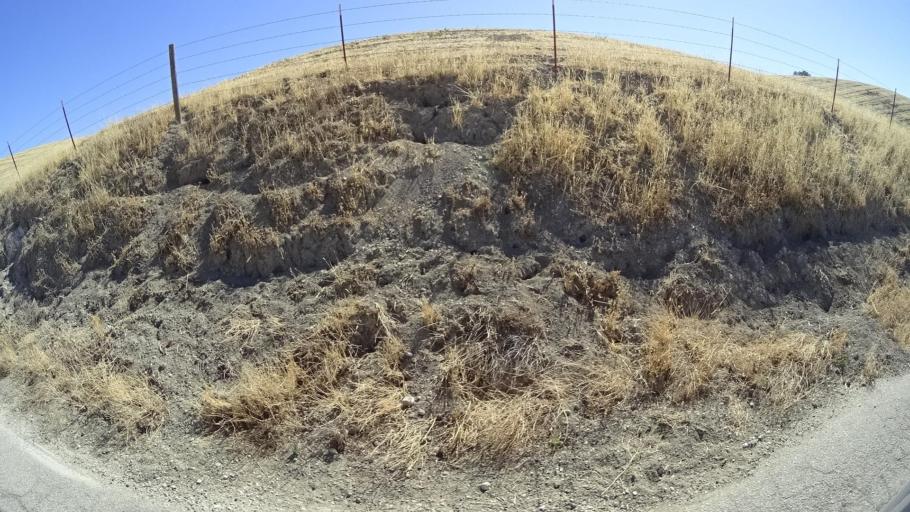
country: US
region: California
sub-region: San Luis Obispo County
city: San Miguel
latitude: 35.7882
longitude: -120.5415
